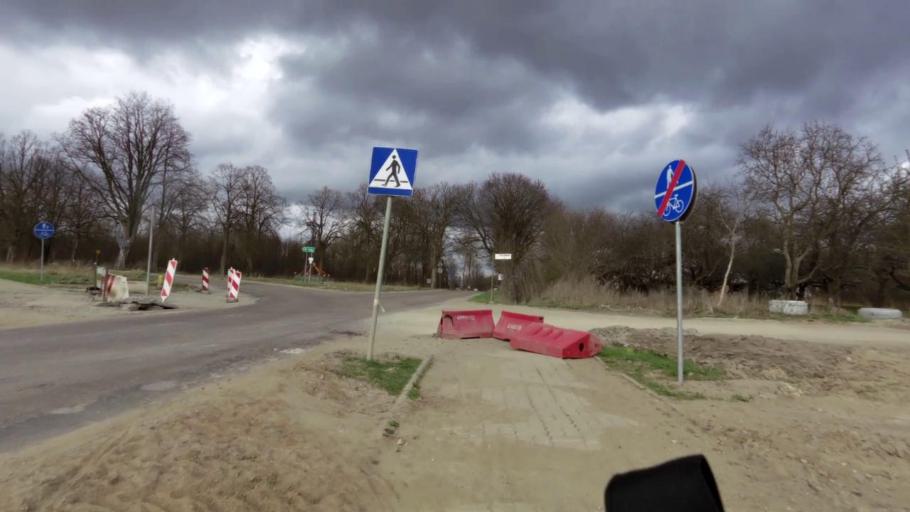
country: PL
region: West Pomeranian Voivodeship
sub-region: Powiat koszalinski
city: Sianow
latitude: 54.2408
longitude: 16.2971
